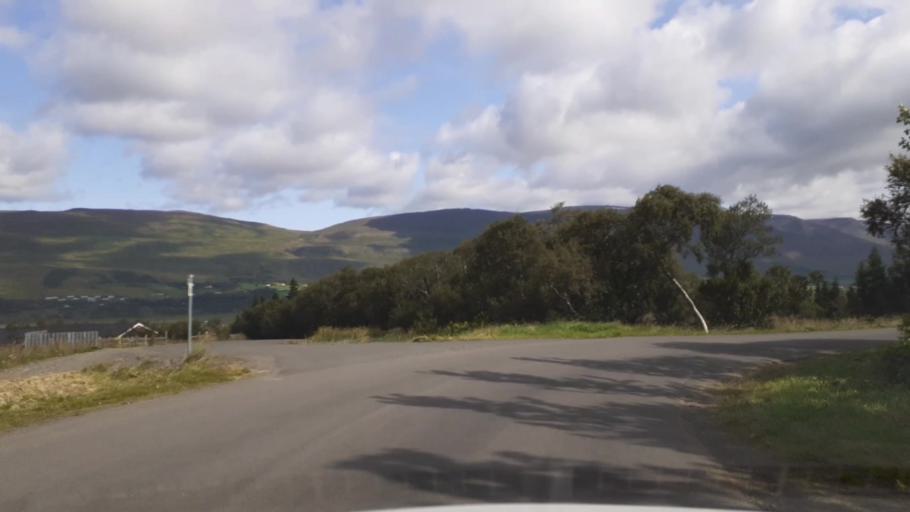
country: IS
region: Northeast
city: Akureyri
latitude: 65.6488
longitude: -18.0883
